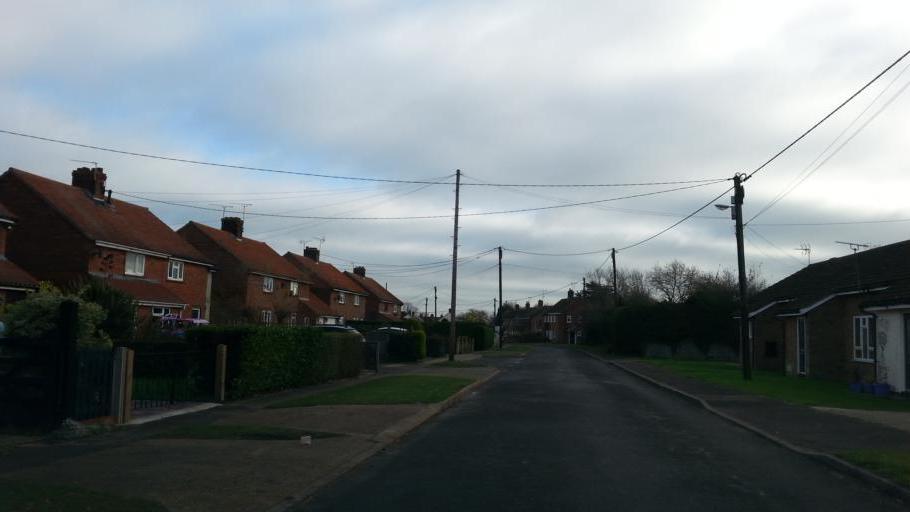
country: GB
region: England
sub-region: Suffolk
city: Framlingham
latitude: 52.2281
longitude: 1.3316
